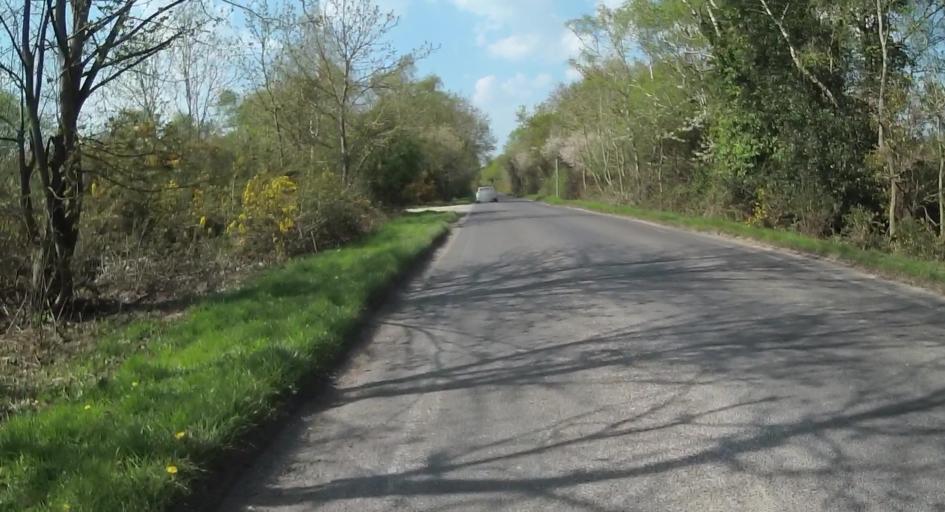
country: GB
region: England
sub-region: Hampshire
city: Tadley
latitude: 51.3553
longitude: -1.1024
